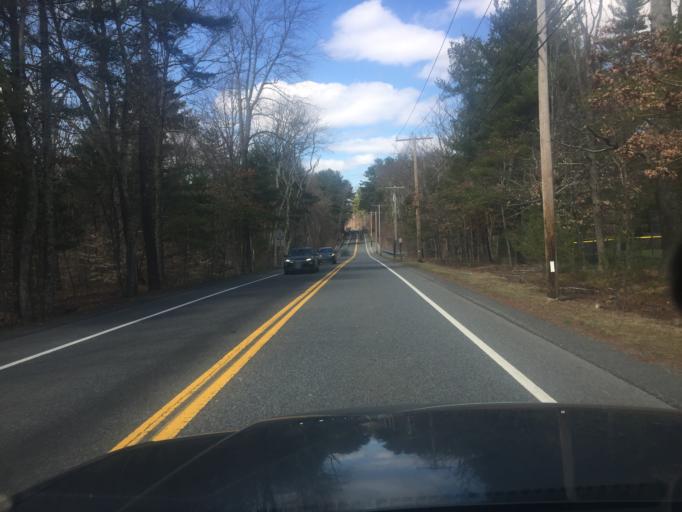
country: US
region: Massachusetts
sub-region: Norfolk County
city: Norfolk
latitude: 42.1040
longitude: -71.3099
